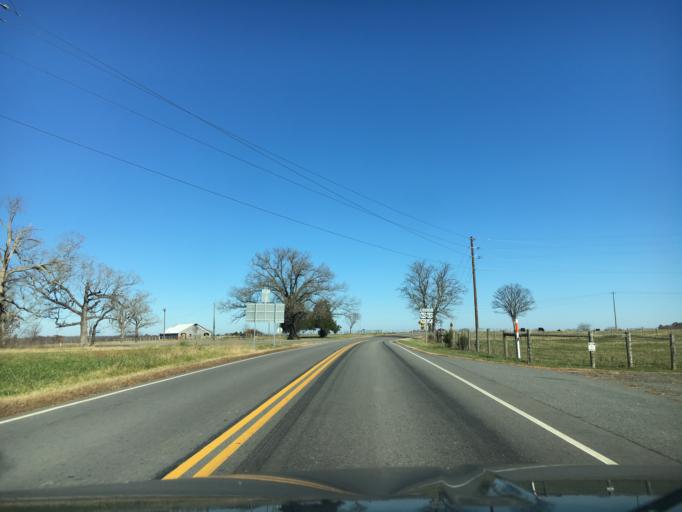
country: US
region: Virginia
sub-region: Buckingham County
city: Buckingham
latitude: 37.5360
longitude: -78.6150
